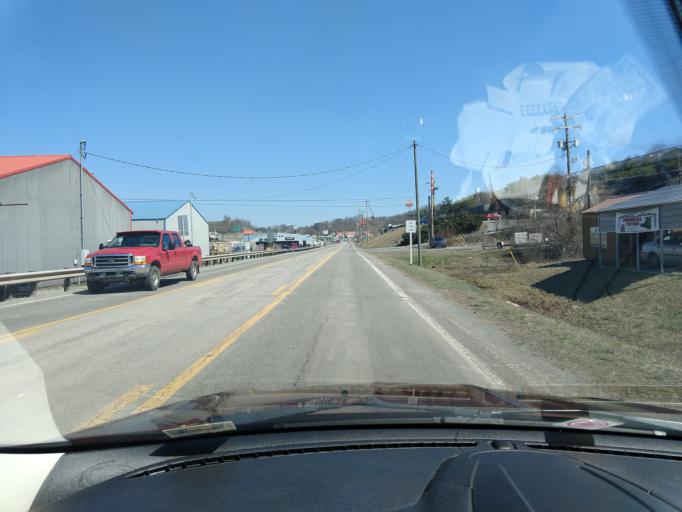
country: US
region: West Virginia
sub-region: Braxton County
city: Sutton
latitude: 38.6973
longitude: -80.6672
